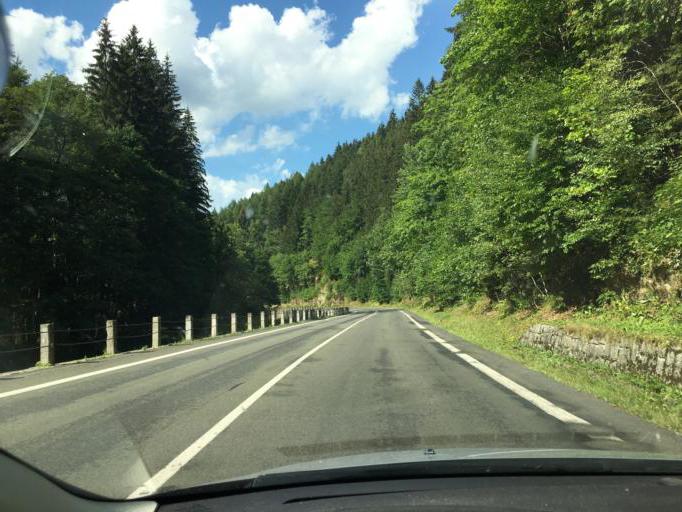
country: CZ
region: Kralovehradecky
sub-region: Okres Trutnov
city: Vrchlabi
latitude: 50.6648
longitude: 15.5940
